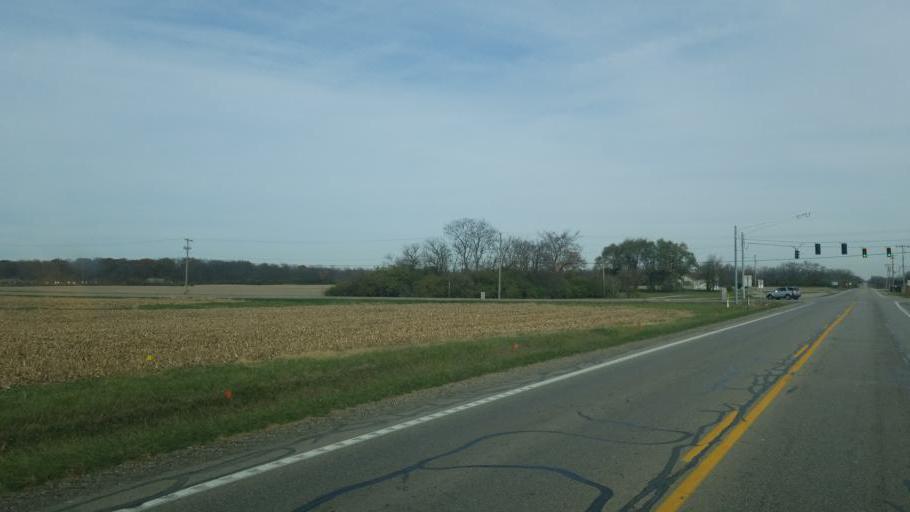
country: US
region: Ohio
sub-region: Madison County
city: West Jefferson
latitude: 39.9658
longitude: -83.3634
